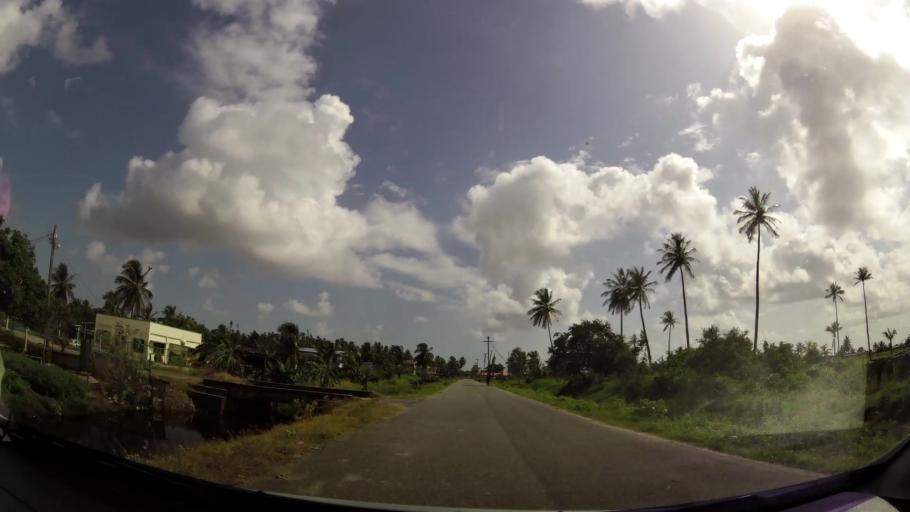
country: GY
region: Demerara-Mahaica
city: Mahaica Village
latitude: 6.7067
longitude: -57.9282
